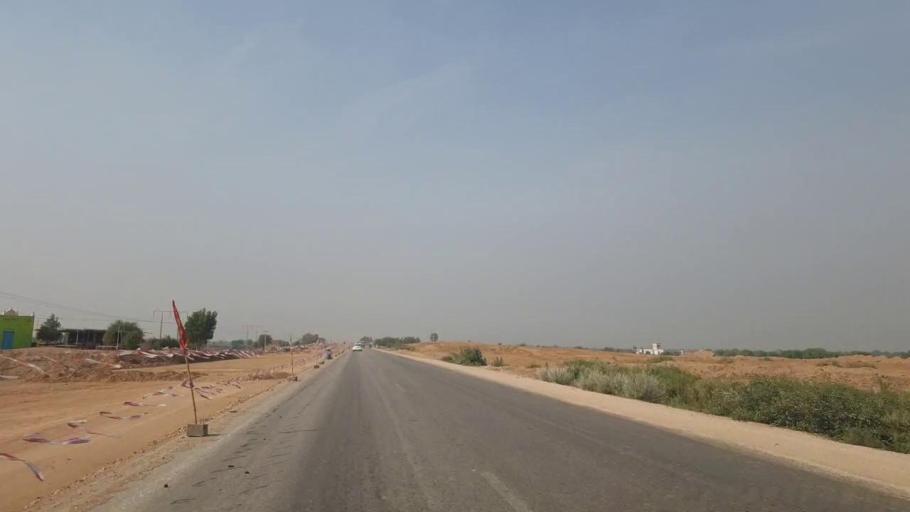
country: PK
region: Sindh
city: Sann
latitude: 26.1297
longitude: 68.0502
